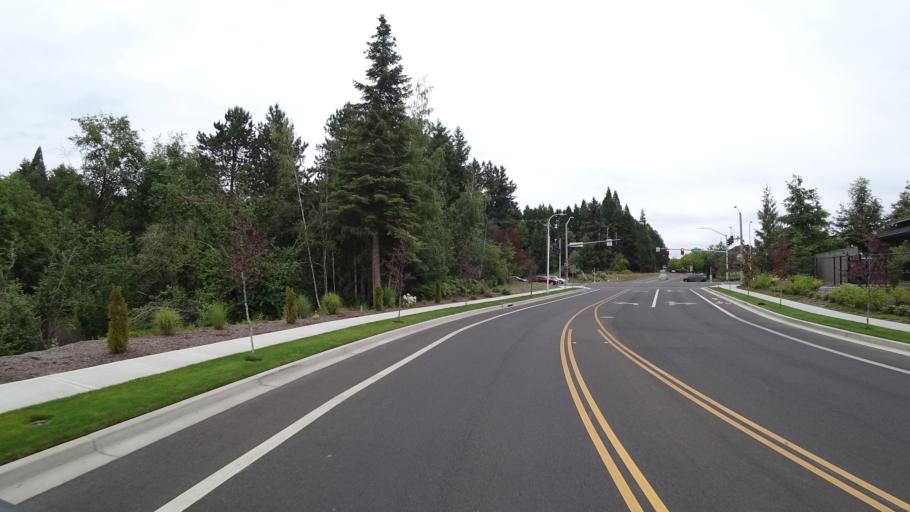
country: US
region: Oregon
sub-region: Washington County
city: Hillsboro
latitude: 45.4938
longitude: -122.9408
